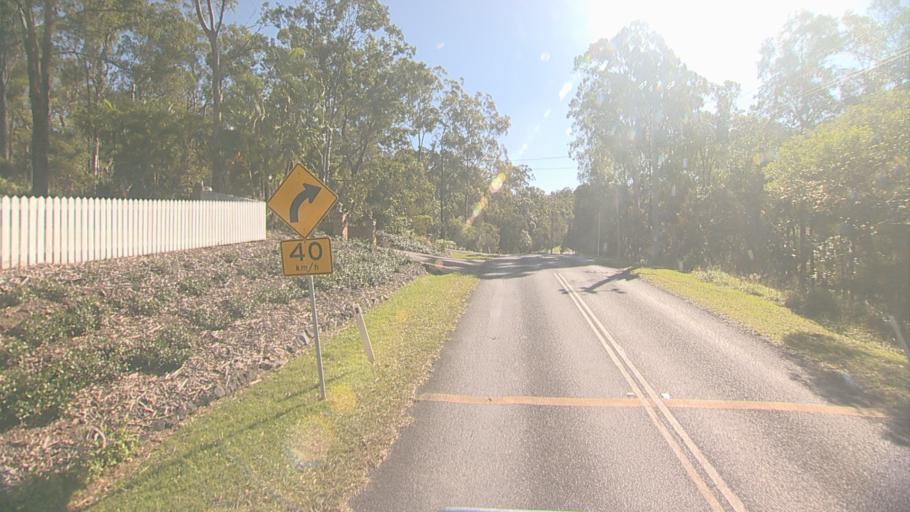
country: AU
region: Queensland
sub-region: Logan
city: Springwood
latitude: -27.6012
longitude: 153.1677
